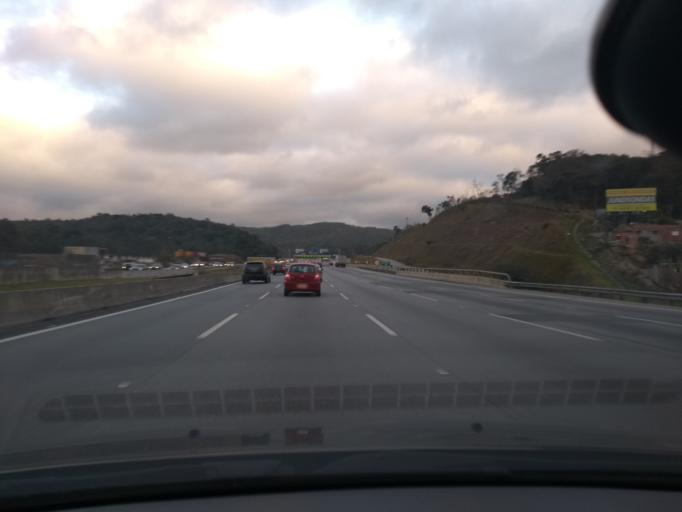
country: BR
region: Sao Paulo
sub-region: Cajamar
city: Cajamar
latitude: -23.3417
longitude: -46.8190
